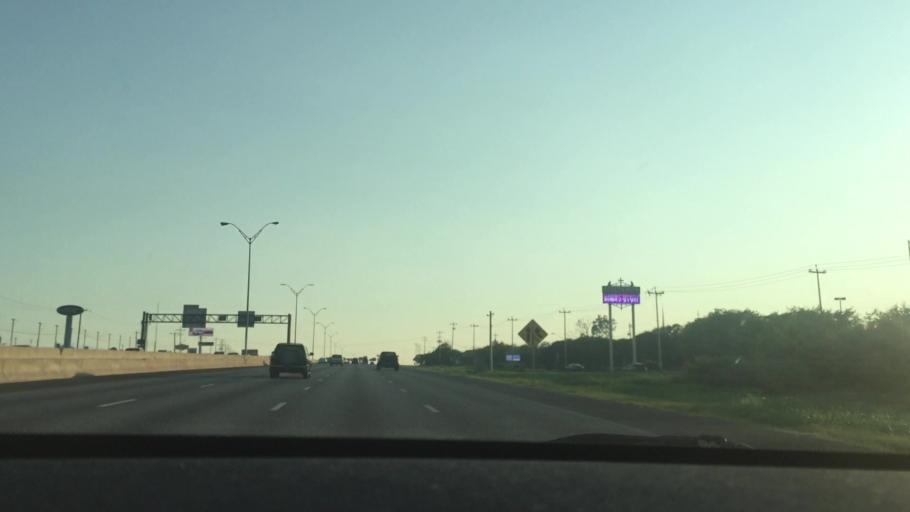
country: US
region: Texas
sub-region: Bexar County
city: Live Oak
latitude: 29.5602
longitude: -98.3423
